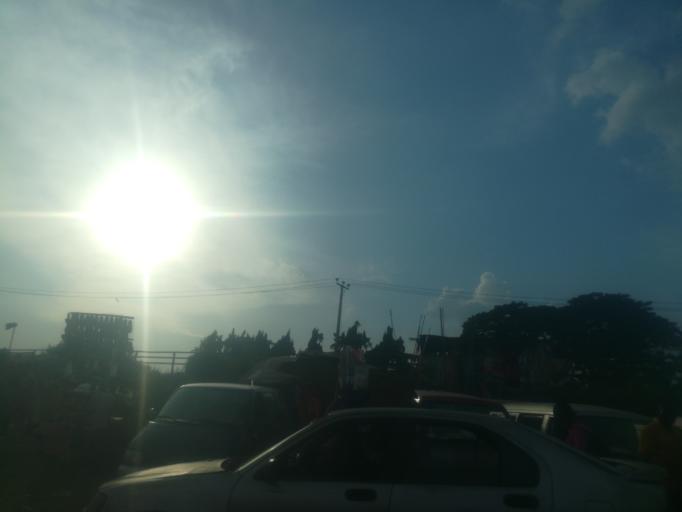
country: NG
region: Ogun
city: Abeokuta
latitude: 7.1576
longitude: 3.3259
